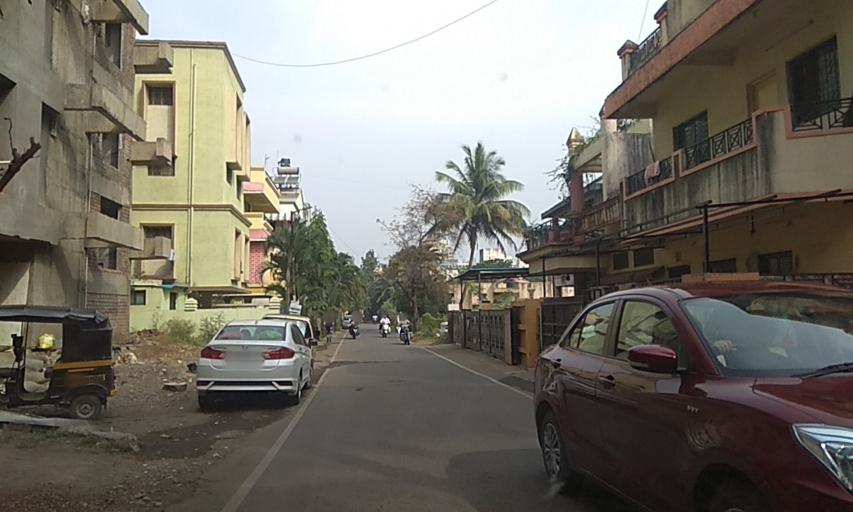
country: IN
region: Maharashtra
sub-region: Pune Division
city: Pune
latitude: 18.5031
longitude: 73.9317
